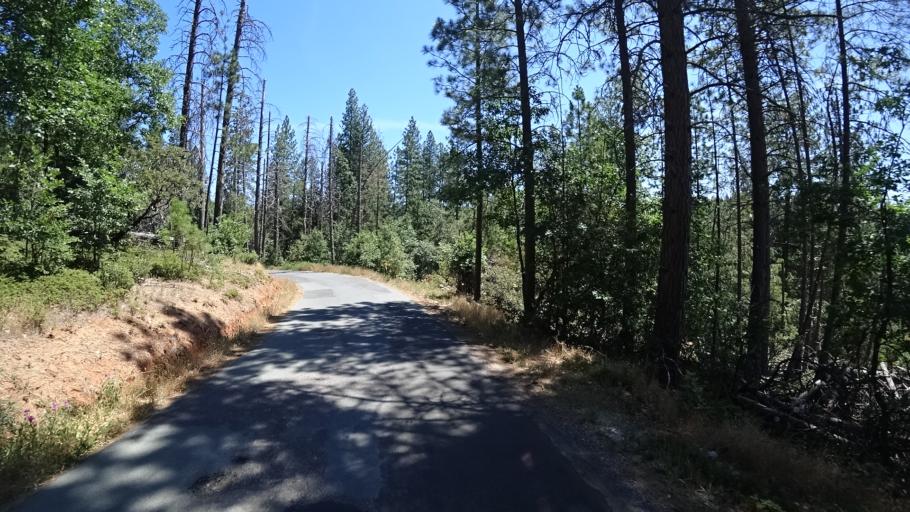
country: US
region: California
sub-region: Amador County
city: Pioneer
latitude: 38.4246
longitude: -120.5140
